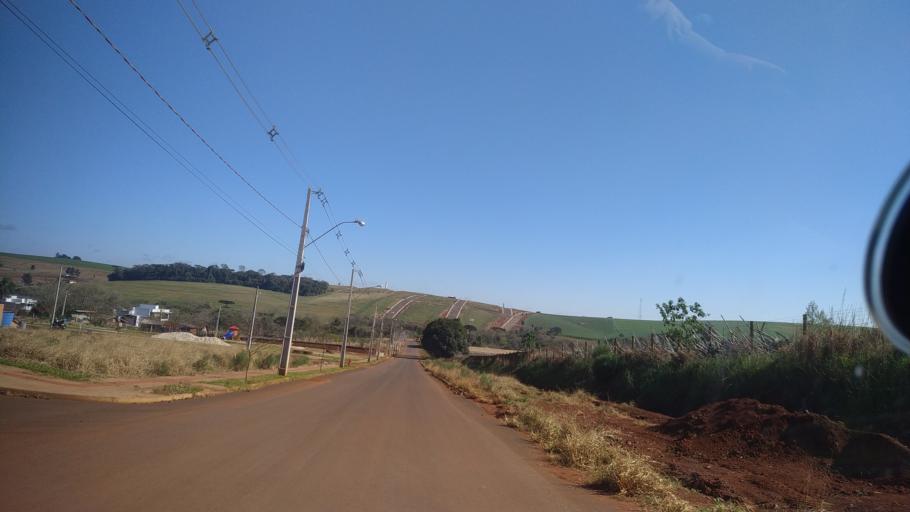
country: BR
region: Santa Catarina
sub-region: Chapeco
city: Chapeco
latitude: -27.0834
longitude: -52.6946
